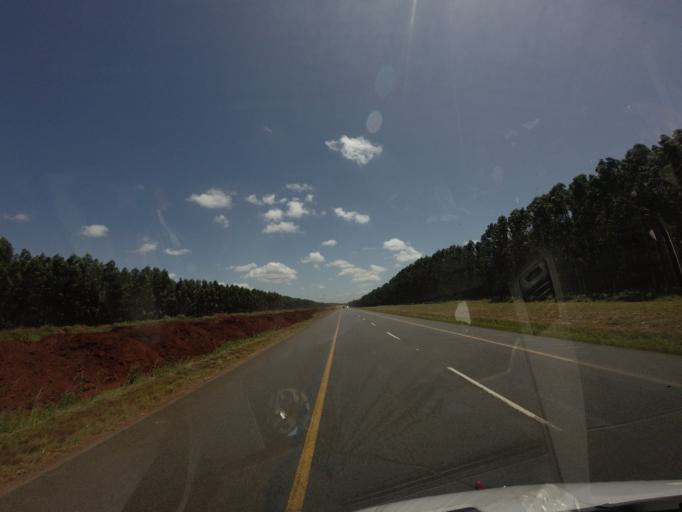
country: ZA
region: KwaZulu-Natal
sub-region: uThungulu District Municipality
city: Empangeni
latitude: -28.7527
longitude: 31.9355
